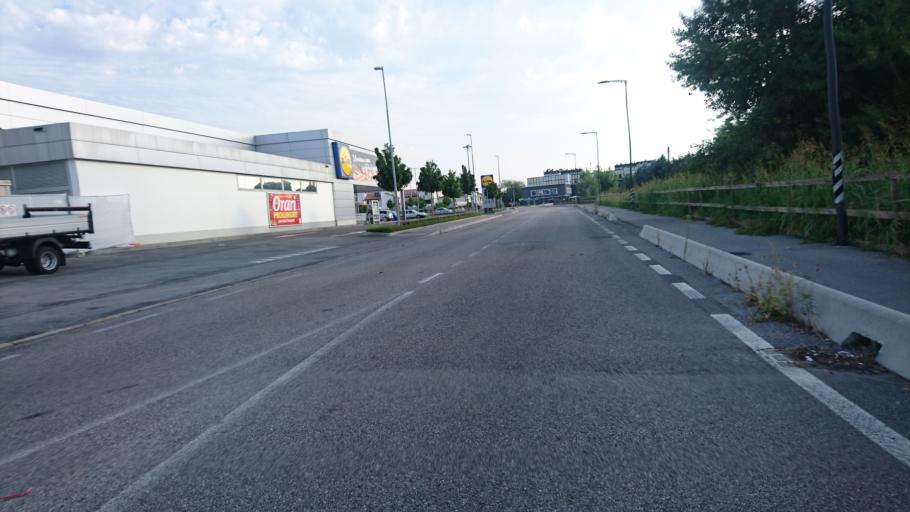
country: IT
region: Veneto
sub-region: Provincia di Padova
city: San Vito
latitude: 45.4255
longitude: 11.9614
